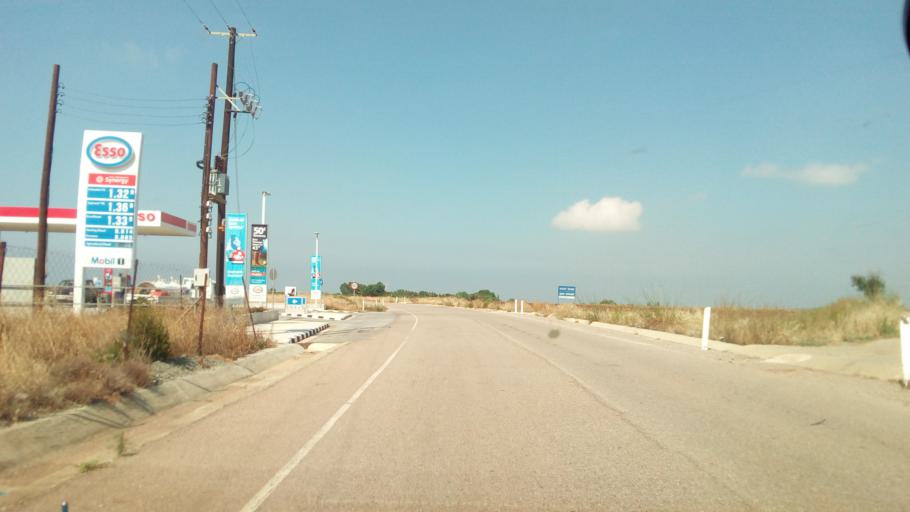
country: CY
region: Limassol
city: Pissouri
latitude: 34.7266
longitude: 32.5695
